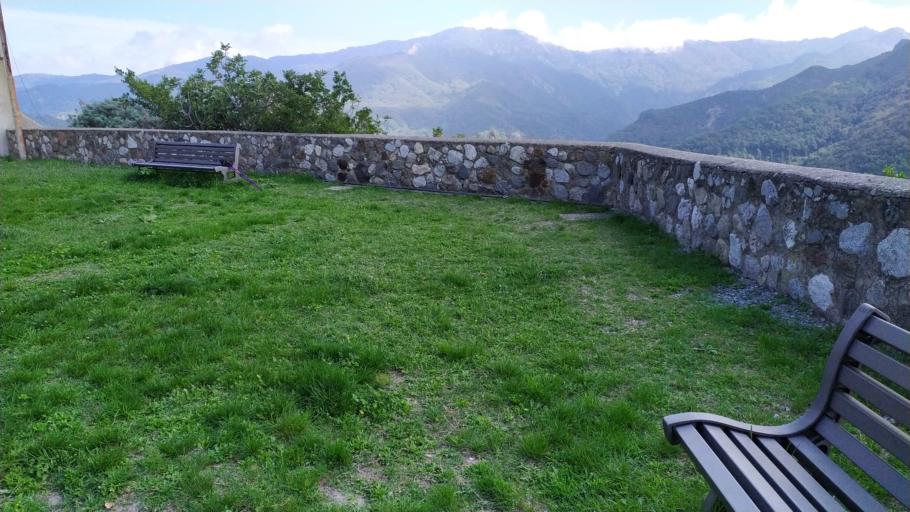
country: IT
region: Sicily
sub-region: Messina
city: Rometta
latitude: 38.1695
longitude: 15.4153
